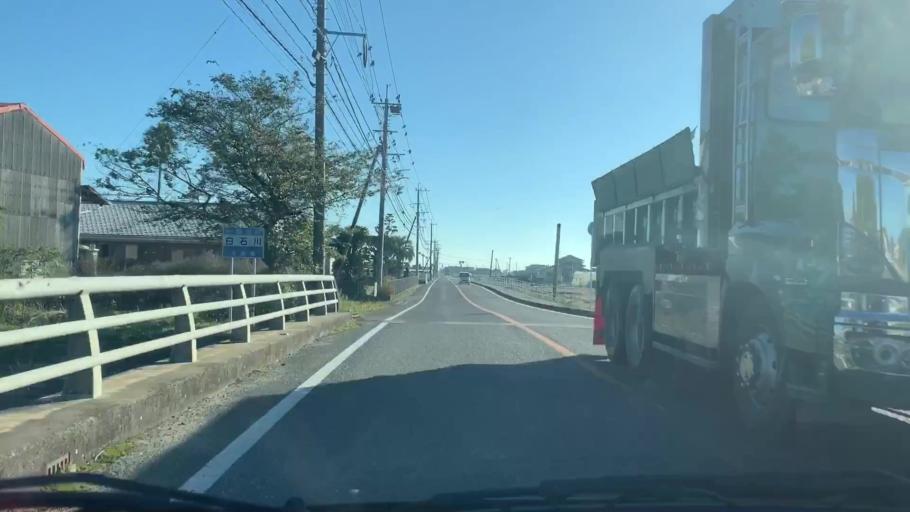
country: JP
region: Saga Prefecture
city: Kashima
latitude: 33.1852
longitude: 130.1550
